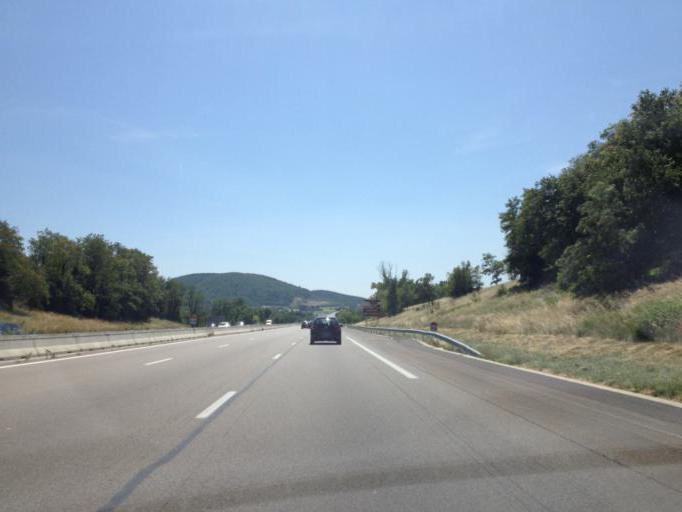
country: FR
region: Rhone-Alpes
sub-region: Departement de la Drome
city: Montboucher-sur-Jabron
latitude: 44.5497
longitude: 4.8096
